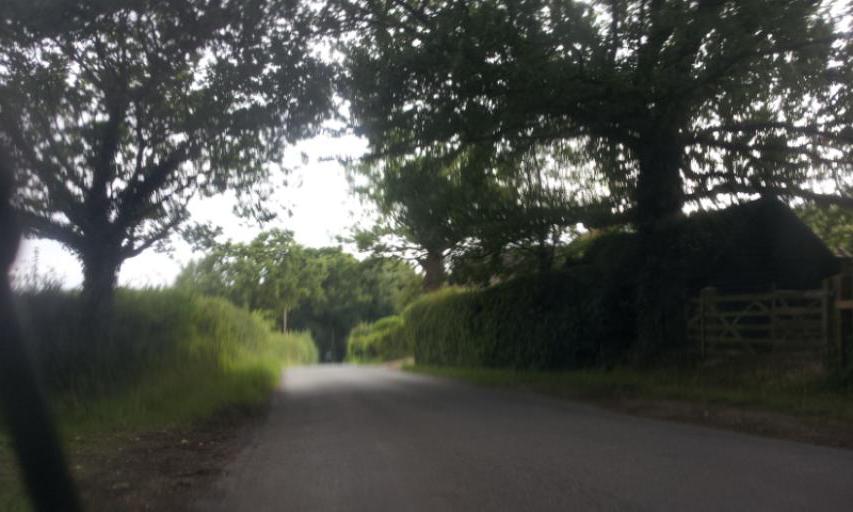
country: GB
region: England
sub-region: Kent
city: Hadlow
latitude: 51.2433
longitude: 0.3026
